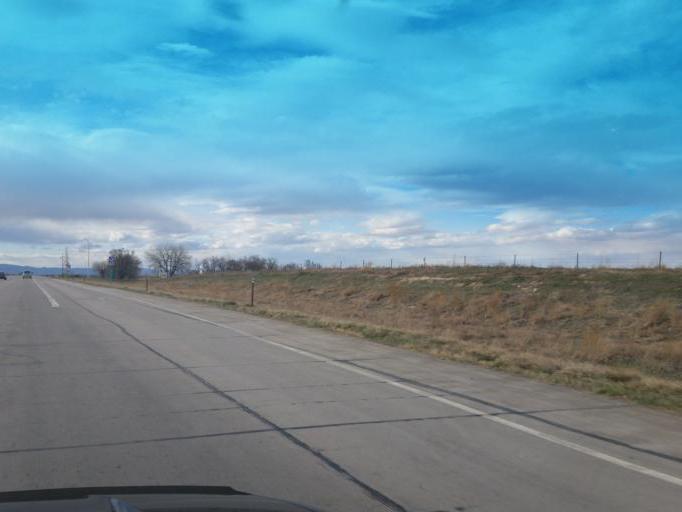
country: US
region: Colorado
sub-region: Weld County
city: Milliken
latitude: 40.3995
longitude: -104.8110
